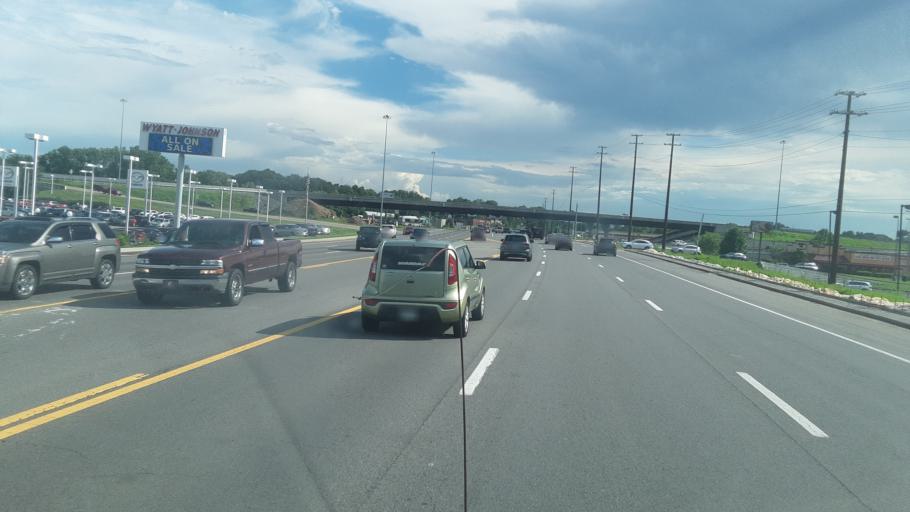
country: US
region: Tennessee
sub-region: Montgomery County
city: Clarksville
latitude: 36.5748
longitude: -87.3025
